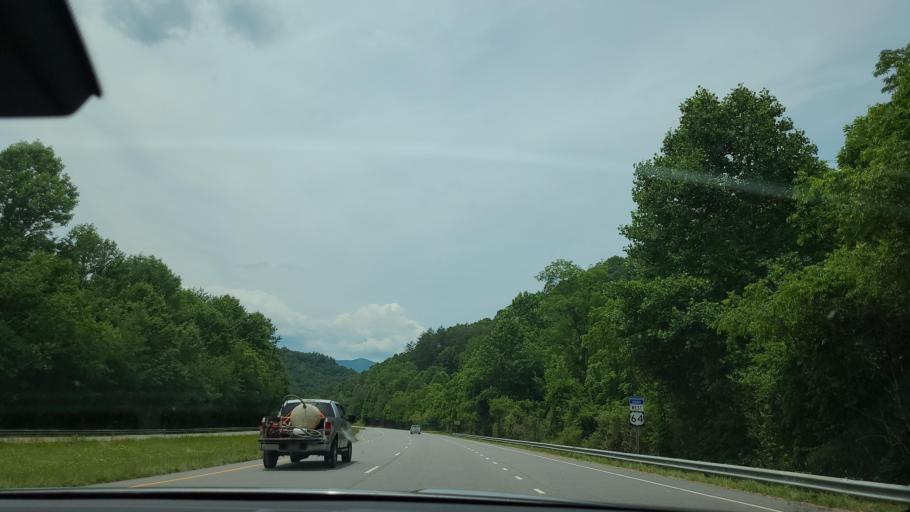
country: US
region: North Carolina
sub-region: Macon County
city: Franklin
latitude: 35.1571
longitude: -83.4597
